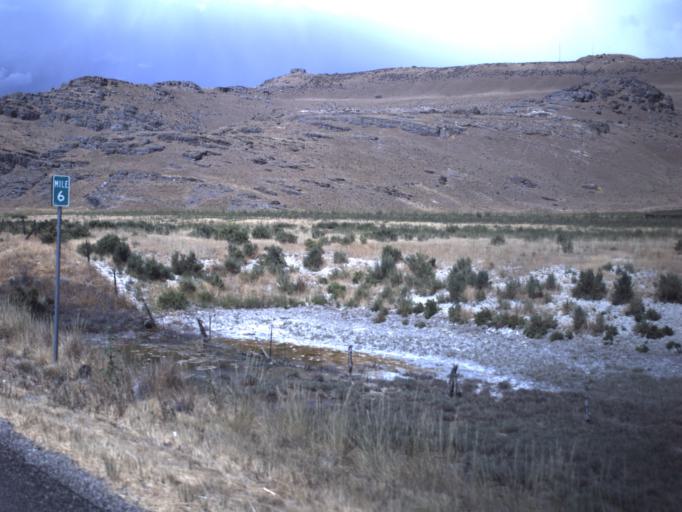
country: US
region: Utah
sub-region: Box Elder County
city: Elwood
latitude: 41.5781
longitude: -112.2410
